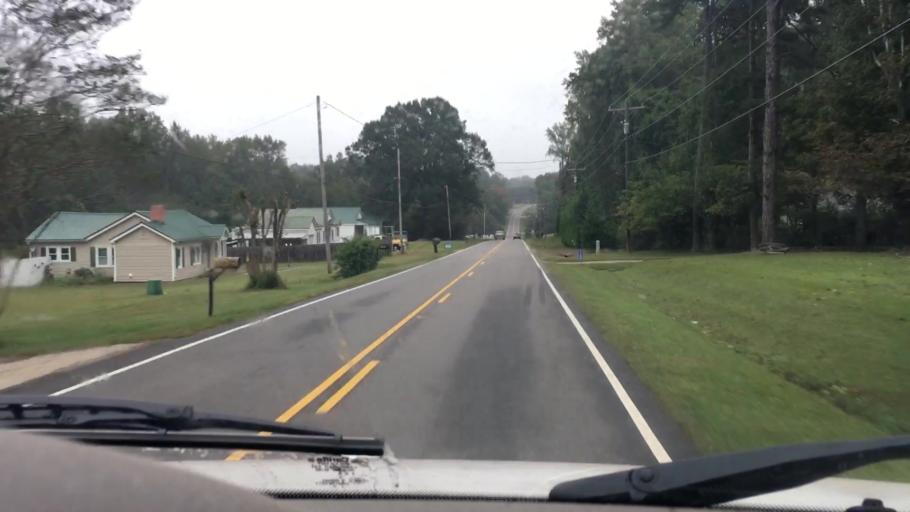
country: US
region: North Carolina
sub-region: Iredell County
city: Mooresville
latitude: 35.6313
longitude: -80.7784
